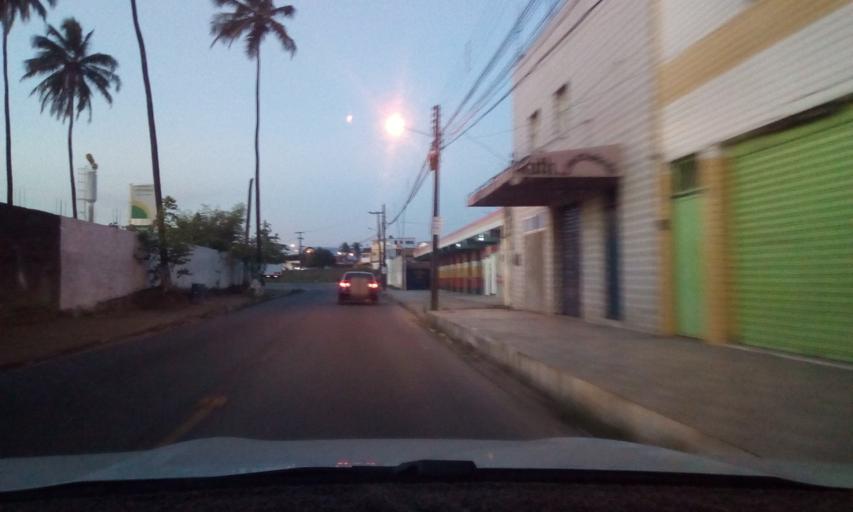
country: BR
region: Paraiba
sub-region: Bayeux
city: Bayeux
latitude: -7.1612
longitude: -34.9060
